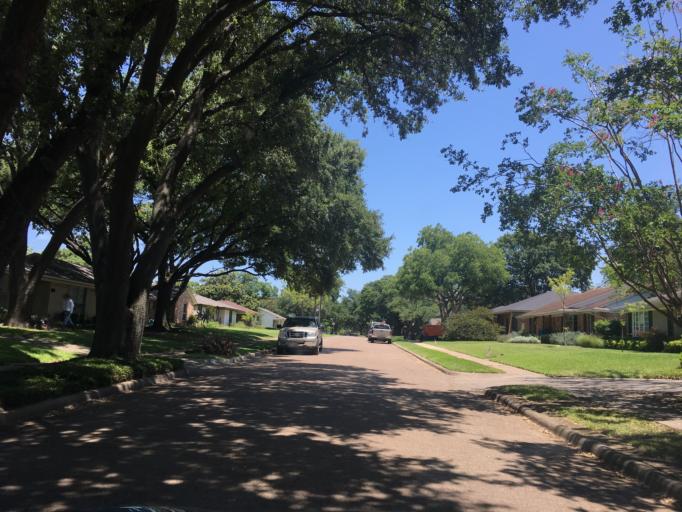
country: US
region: Texas
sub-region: Dallas County
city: Highland Park
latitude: 32.8387
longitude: -96.7415
